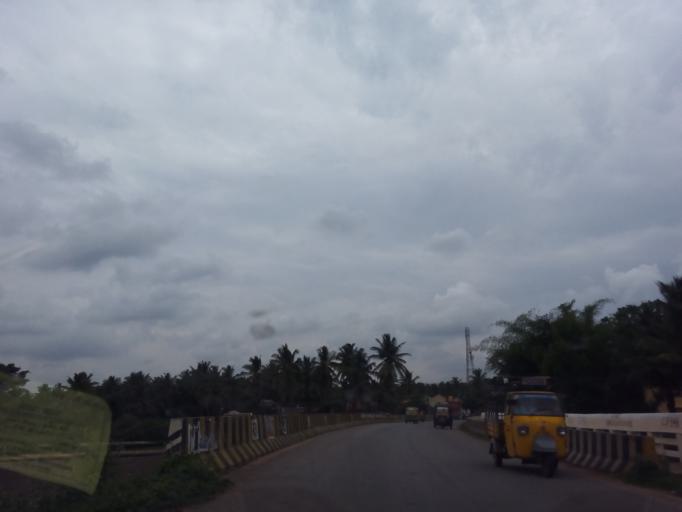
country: IN
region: Karnataka
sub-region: Hassan
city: Channarayapatna
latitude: 12.8819
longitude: 76.4173
